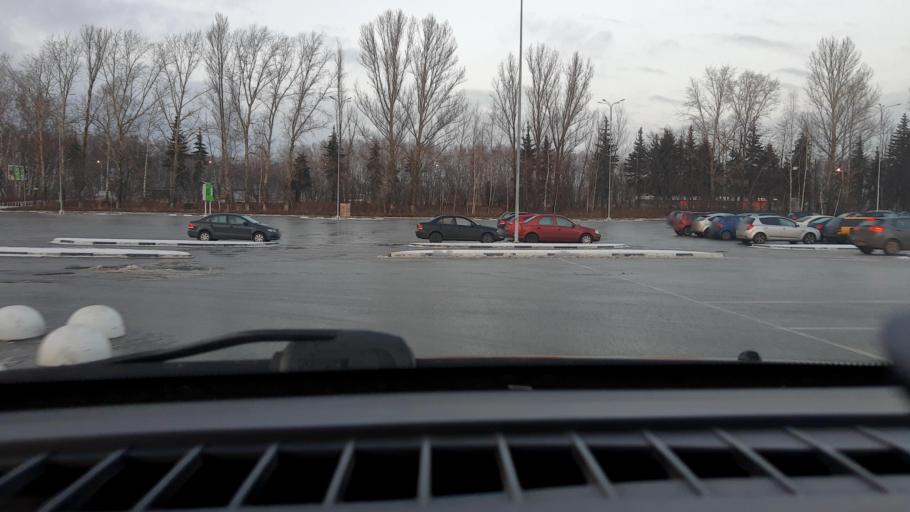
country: RU
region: Nizjnij Novgorod
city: Gorbatovka
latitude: 56.3082
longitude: 43.7719
